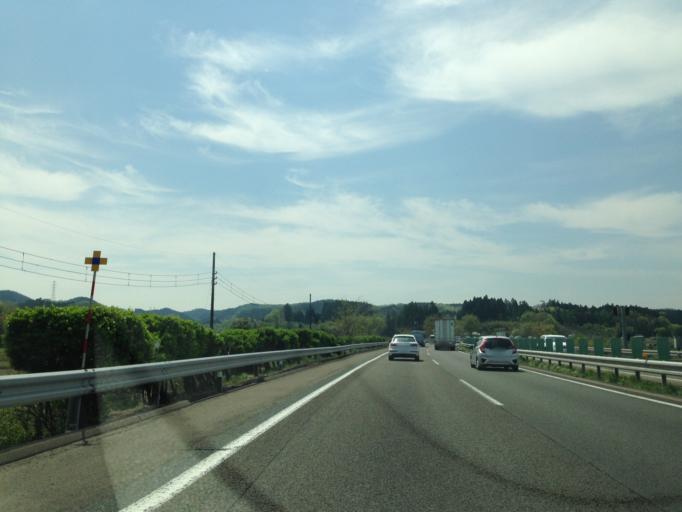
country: JP
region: Miyagi
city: Iwanuma
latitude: 38.1745
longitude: 140.7702
